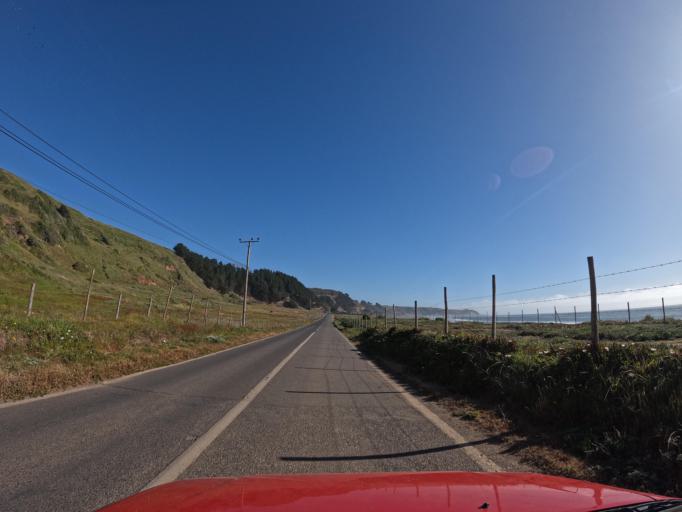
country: CL
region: Maule
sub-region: Provincia de Talca
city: Constitucion
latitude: -34.8629
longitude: -72.1476
